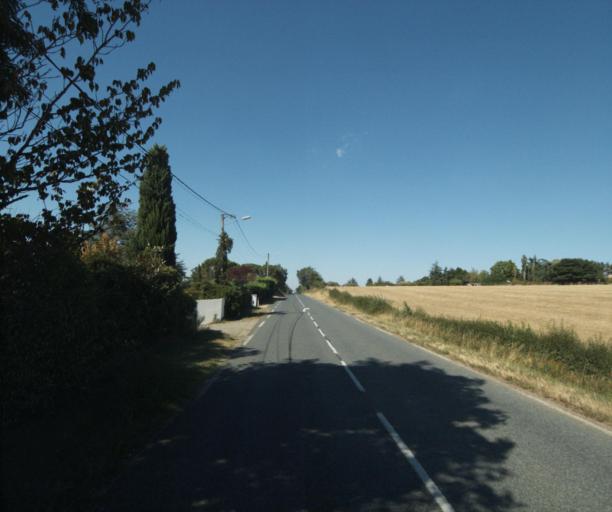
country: FR
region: Rhone-Alpes
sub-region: Departement du Rhone
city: La Tour-de-Salvagny
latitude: 45.8285
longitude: 4.6967
